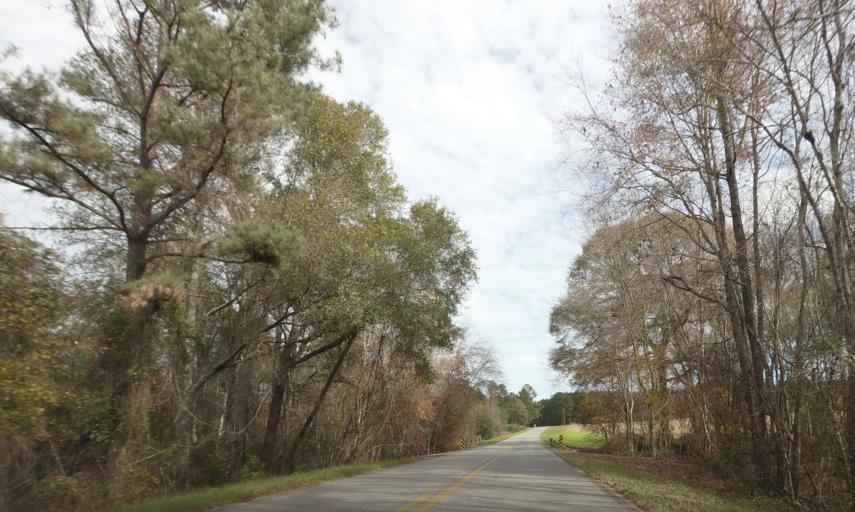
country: US
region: Georgia
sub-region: Dodge County
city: Chester
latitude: 32.4556
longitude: -83.1372
